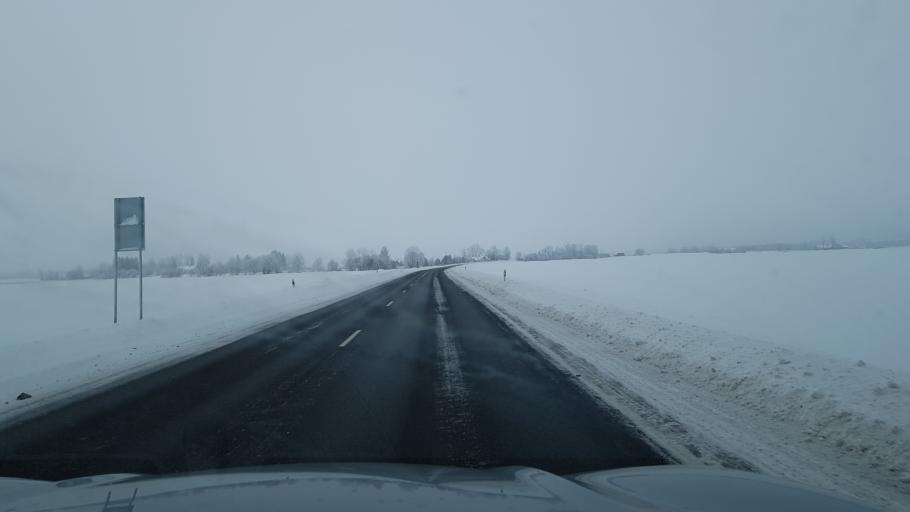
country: EE
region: Ida-Virumaa
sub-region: Johvi vald
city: Johvi
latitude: 59.3121
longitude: 27.3926
